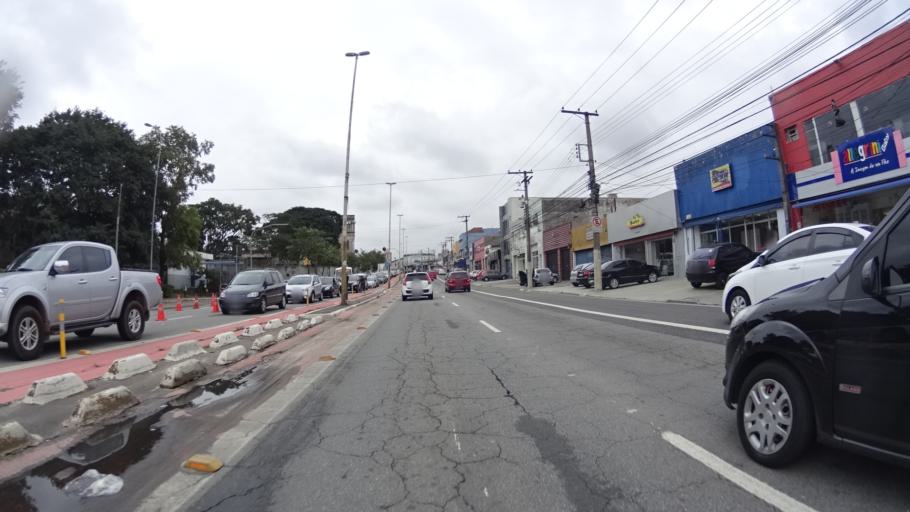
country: BR
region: Sao Paulo
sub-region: Sao Paulo
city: Sao Paulo
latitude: -23.5060
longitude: -46.6153
